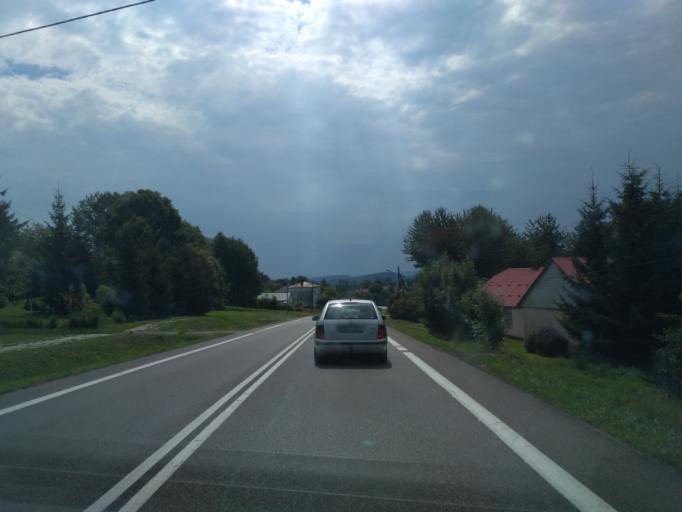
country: PL
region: Subcarpathian Voivodeship
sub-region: Powiat sanocki
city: Strachocina
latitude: 49.6259
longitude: 22.0993
